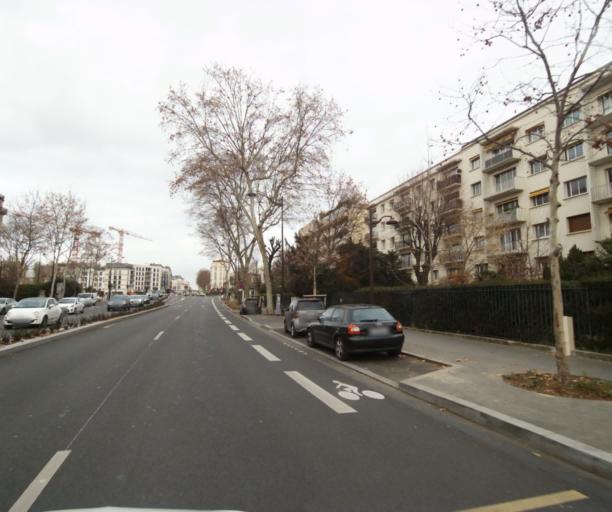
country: FR
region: Ile-de-France
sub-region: Departement des Hauts-de-Seine
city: Neuilly-sur-Seine
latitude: 48.8926
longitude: 2.2686
